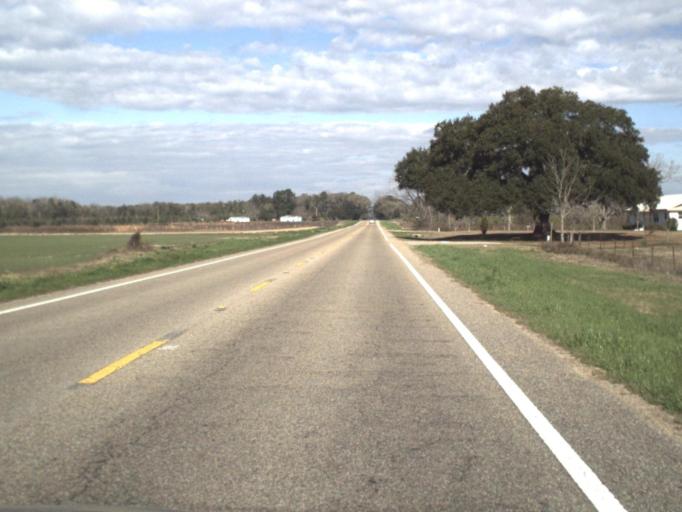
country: US
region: Florida
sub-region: Jackson County
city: Malone
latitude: 30.9784
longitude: -85.1741
